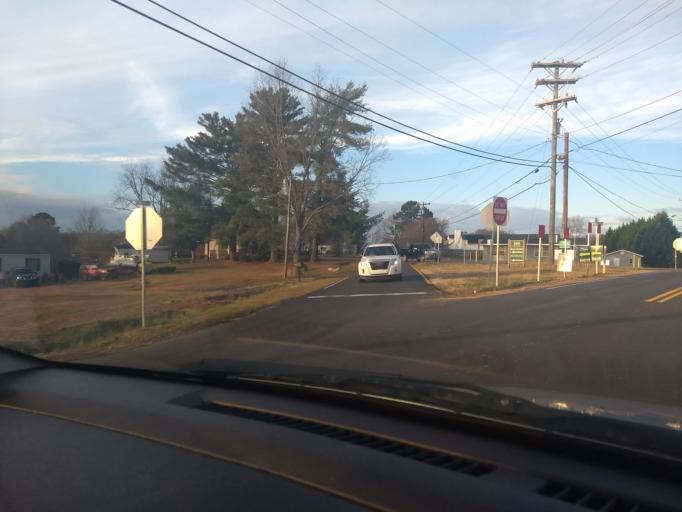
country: US
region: South Carolina
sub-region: Greenville County
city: Greer
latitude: 34.9769
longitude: -82.1943
